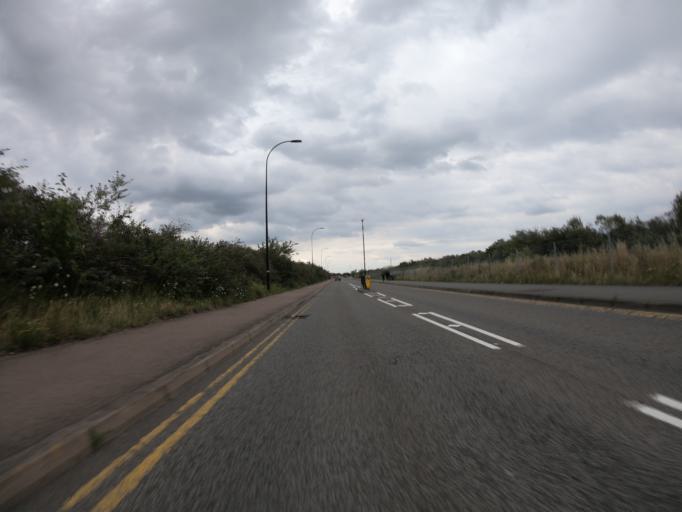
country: GB
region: England
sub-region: Greater London
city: Woolwich
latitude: 51.5105
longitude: 0.0770
